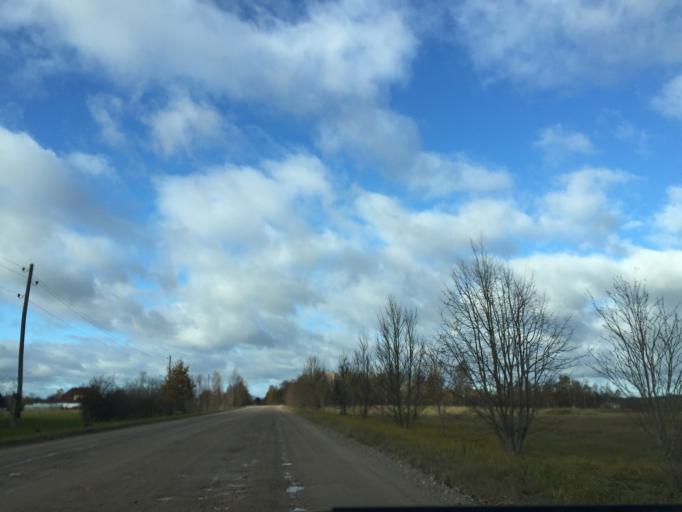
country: LV
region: Tukuma Rajons
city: Tukums
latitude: 56.9646
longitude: 23.2404
